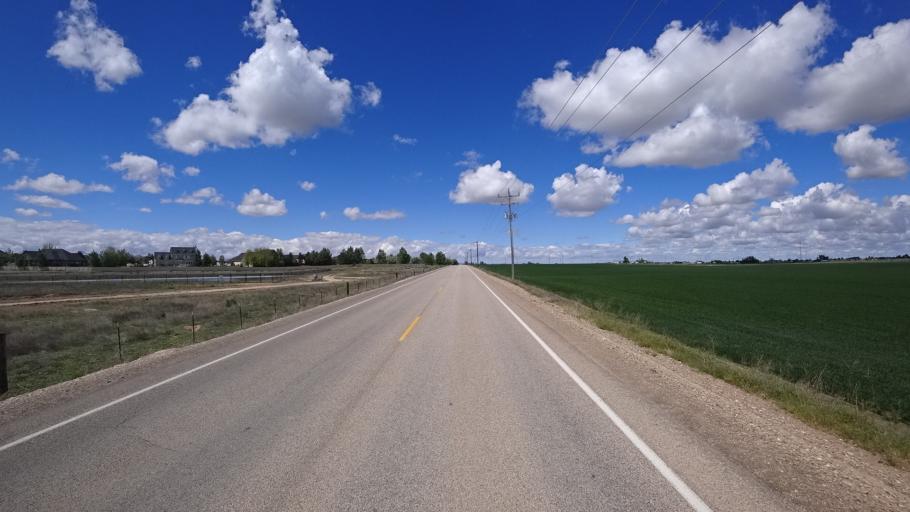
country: US
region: Idaho
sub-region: Ada County
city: Kuna
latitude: 43.4591
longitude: -116.3254
